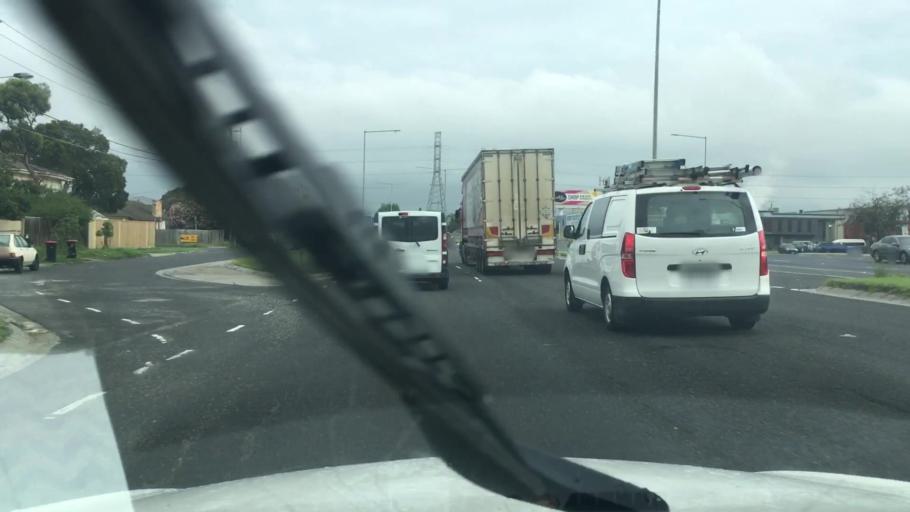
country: AU
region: Victoria
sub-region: Greater Dandenong
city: Springvale
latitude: -37.9431
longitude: 145.1400
